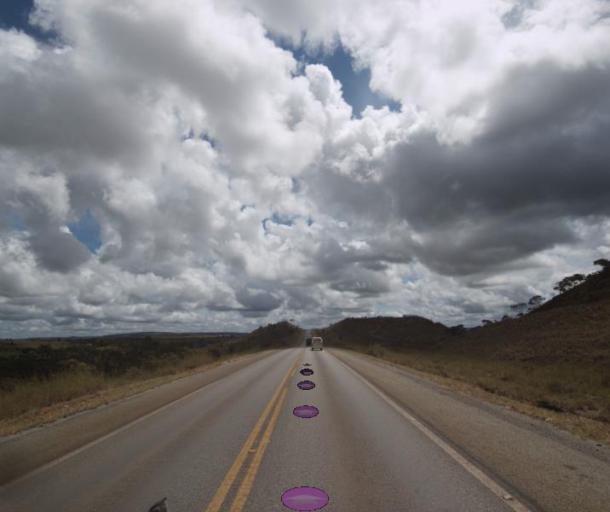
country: BR
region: Goias
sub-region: Pirenopolis
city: Pirenopolis
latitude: -15.7626
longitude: -48.7309
